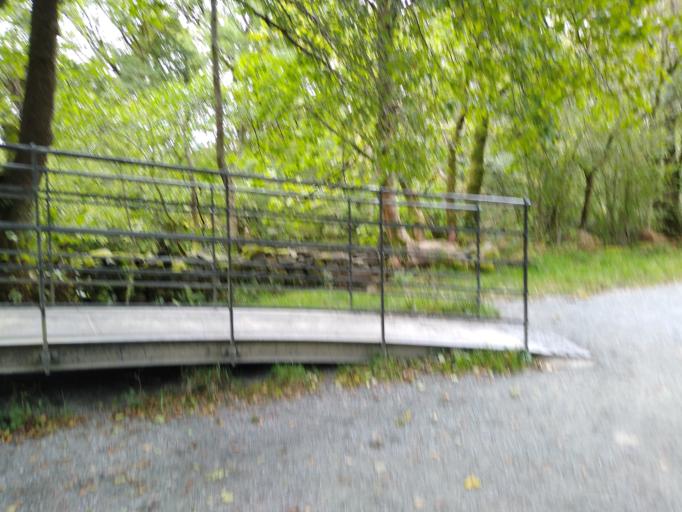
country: GB
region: England
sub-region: Cumbria
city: Ambleside
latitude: 54.4485
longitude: -3.0072
